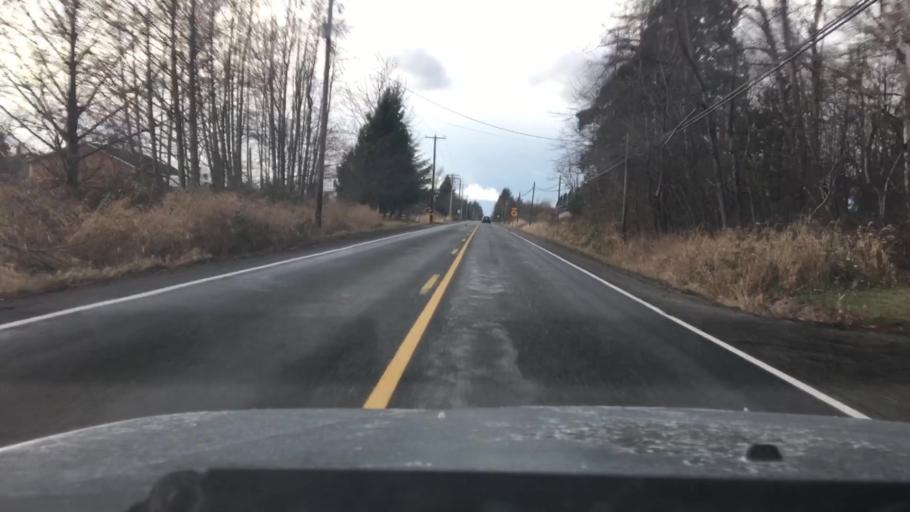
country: US
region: Washington
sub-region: Whatcom County
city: Ferndale
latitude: 48.8483
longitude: -122.6568
